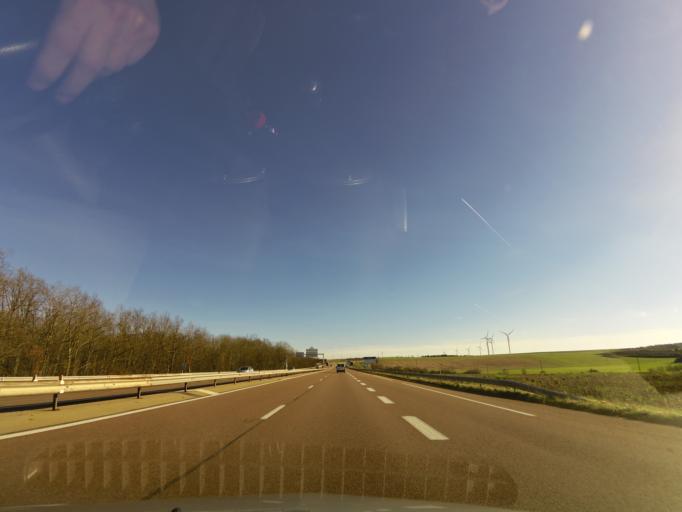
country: FR
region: Bourgogne
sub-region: Departement de l'Yonne
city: Venoy
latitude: 47.7987
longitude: 3.6523
